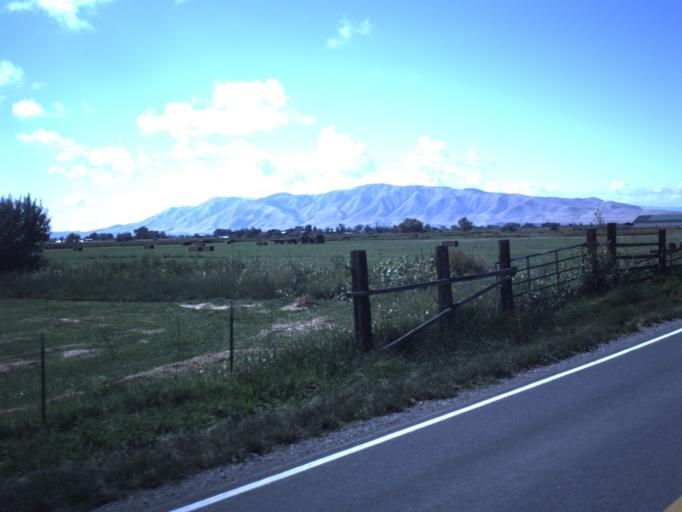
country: US
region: Utah
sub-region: Utah County
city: Spanish Fork
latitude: 40.1584
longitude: -111.6974
